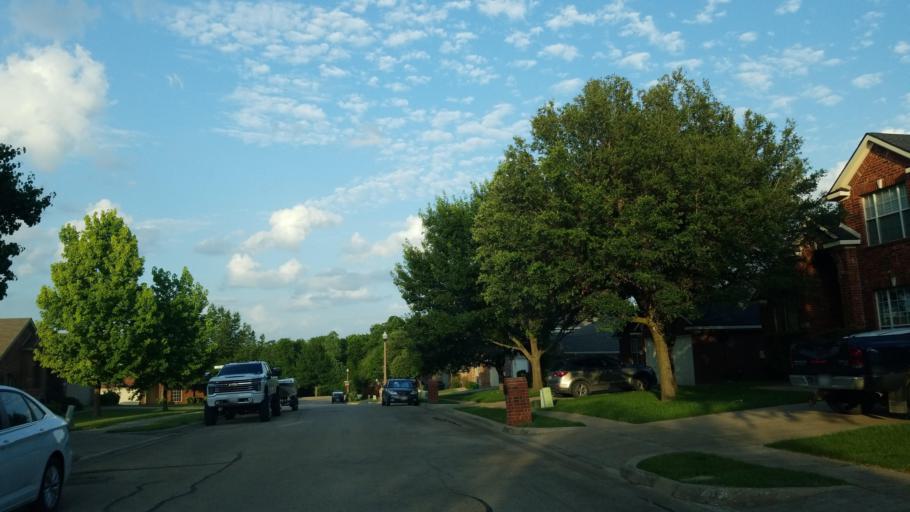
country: US
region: Texas
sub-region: Denton County
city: Corinth
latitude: 33.1485
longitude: -97.1229
